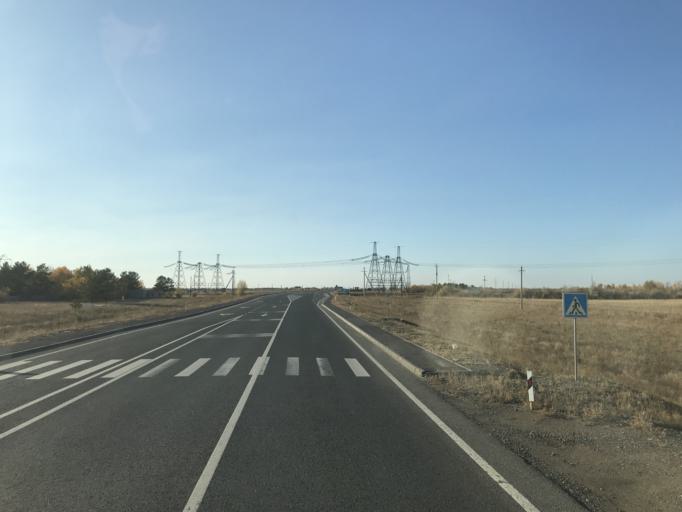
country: KZ
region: Pavlodar
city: Koktobe
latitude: 51.9078
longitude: 77.3631
